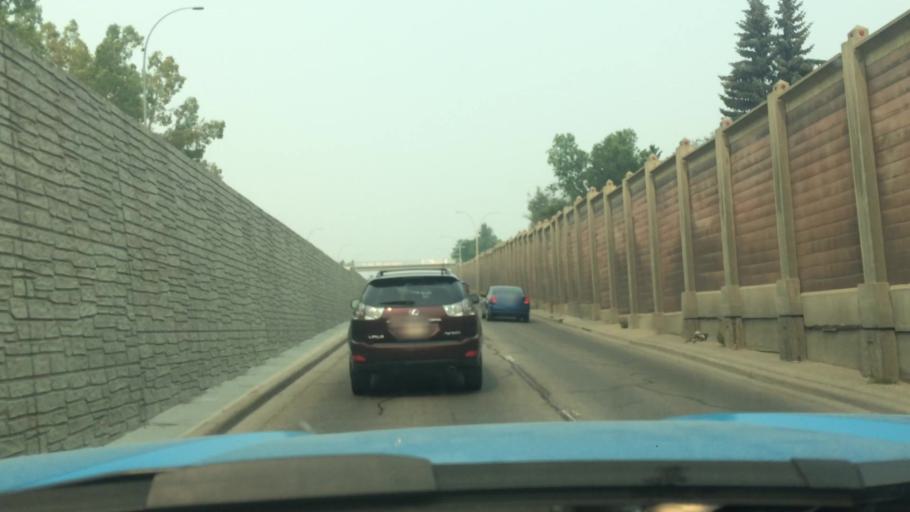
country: CA
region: Alberta
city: Calgary
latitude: 51.0632
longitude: -114.1179
